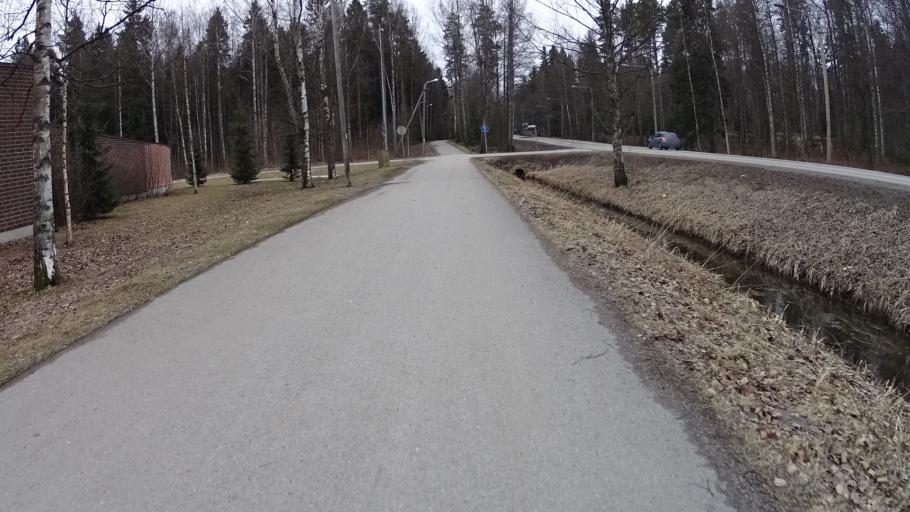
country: FI
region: Uusimaa
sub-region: Helsinki
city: Kilo
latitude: 60.2318
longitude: 24.7533
